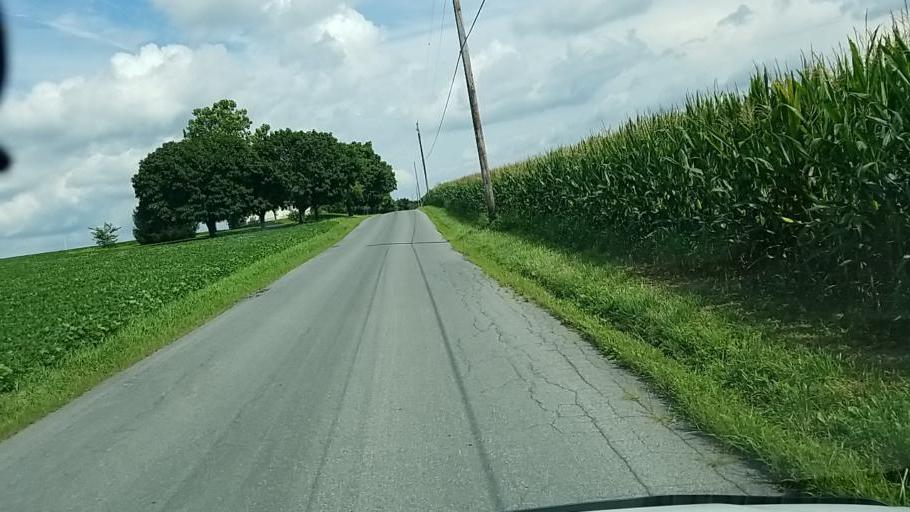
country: US
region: Pennsylvania
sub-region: Dauphin County
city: Elizabethville
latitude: 40.6121
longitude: -76.8341
